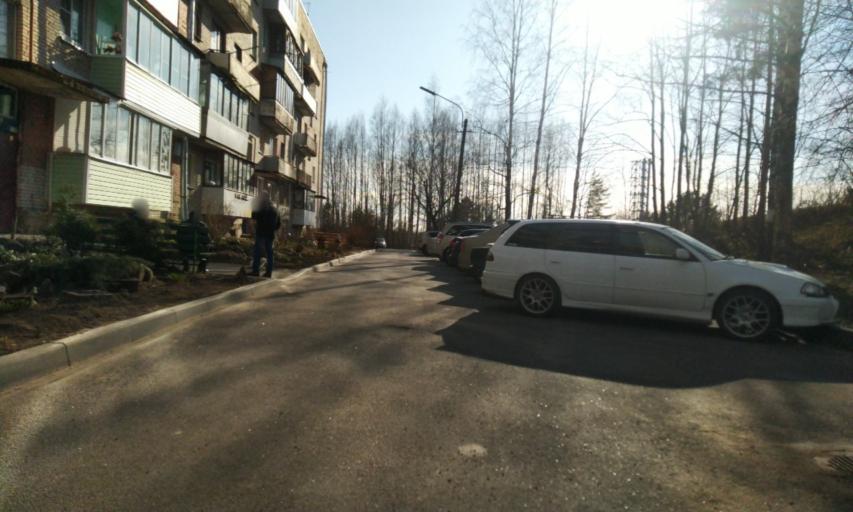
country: RU
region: Leningrad
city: Toksovo
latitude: 60.1247
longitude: 30.5007
